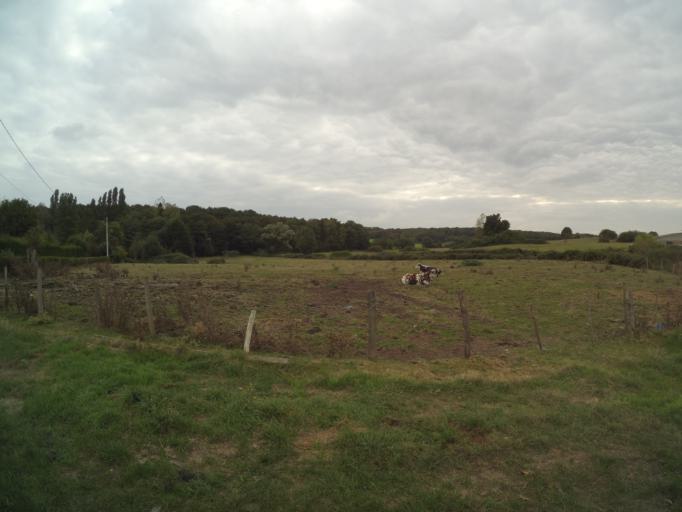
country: FR
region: Centre
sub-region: Departement d'Indre-et-Loire
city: Auzouer-en-Touraine
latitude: 47.5093
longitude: 0.9434
